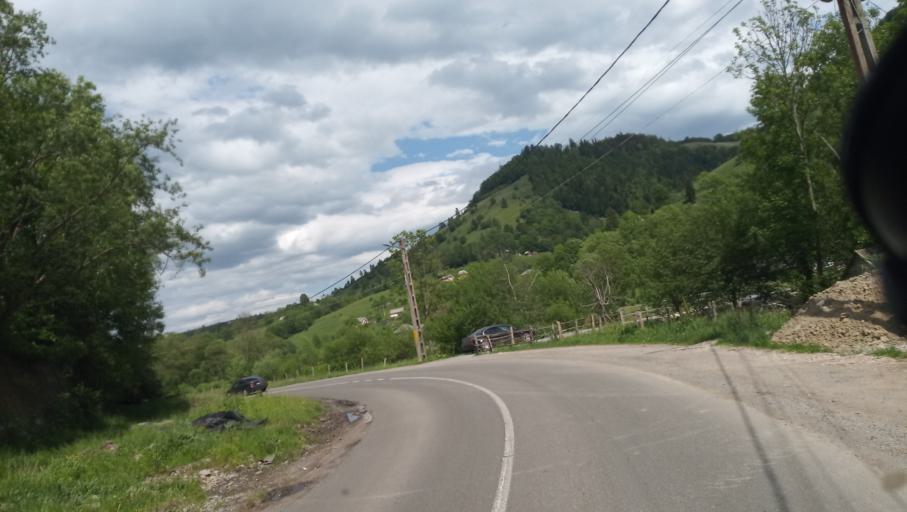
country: RO
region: Alba
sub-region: Comuna Ciuruleasa
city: Ciuruleasa
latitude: 46.2569
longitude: 23.0368
